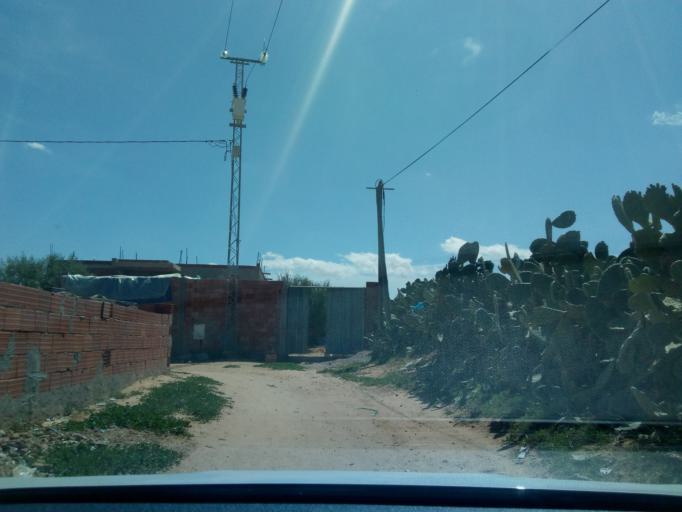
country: TN
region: Safaqis
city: Sfax
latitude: 34.7363
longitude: 10.4962
